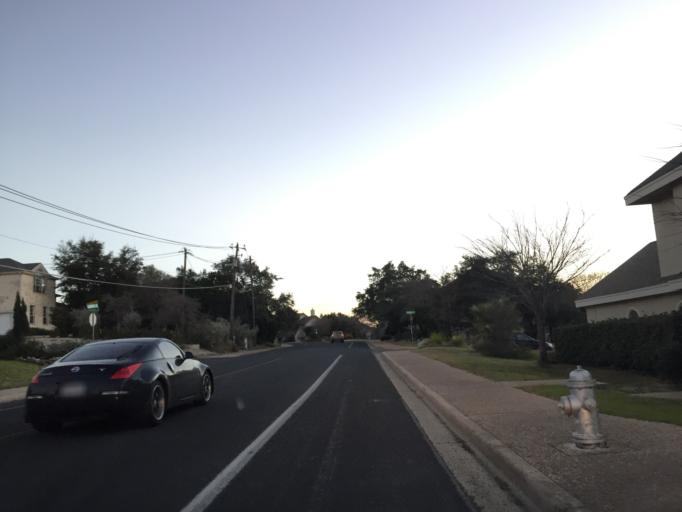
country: US
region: Texas
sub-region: Williamson County
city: Jollyville
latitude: 30.4003
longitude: -97.7676
